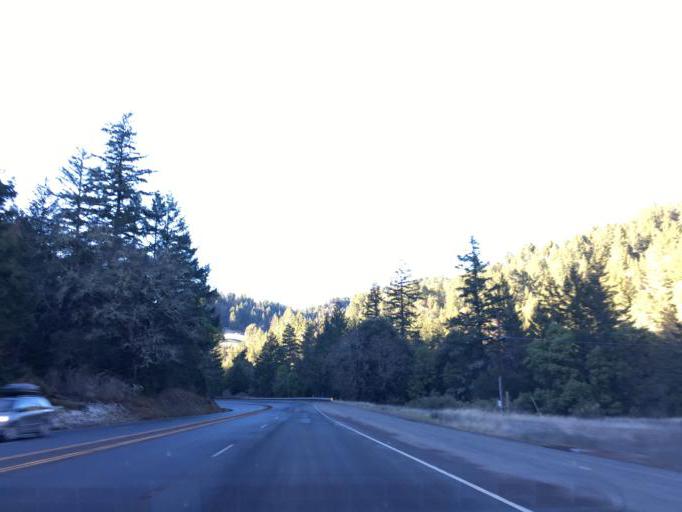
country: US
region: California
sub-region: Mendocino County
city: Laytonville
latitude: 39.8280
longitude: -123.5974
